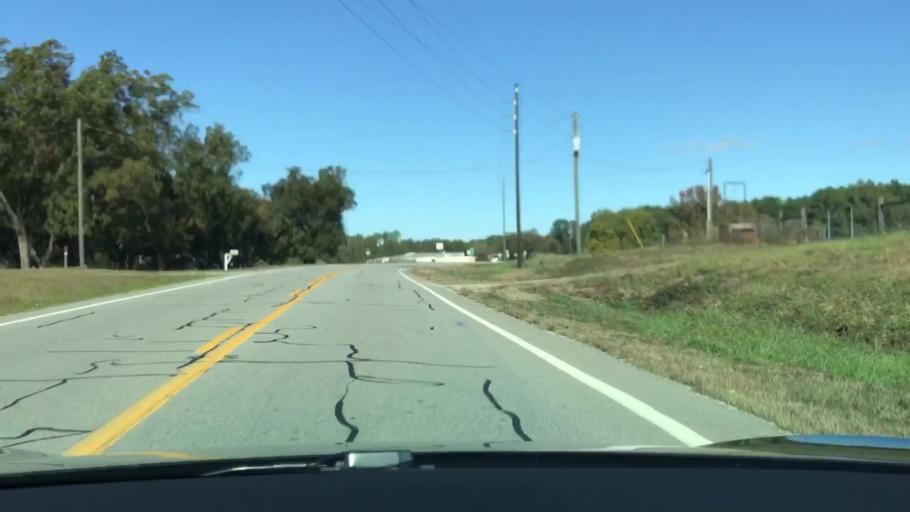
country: US
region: Georgia
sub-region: Warren County
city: Warrenton
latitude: 33.3977
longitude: -82.6535
